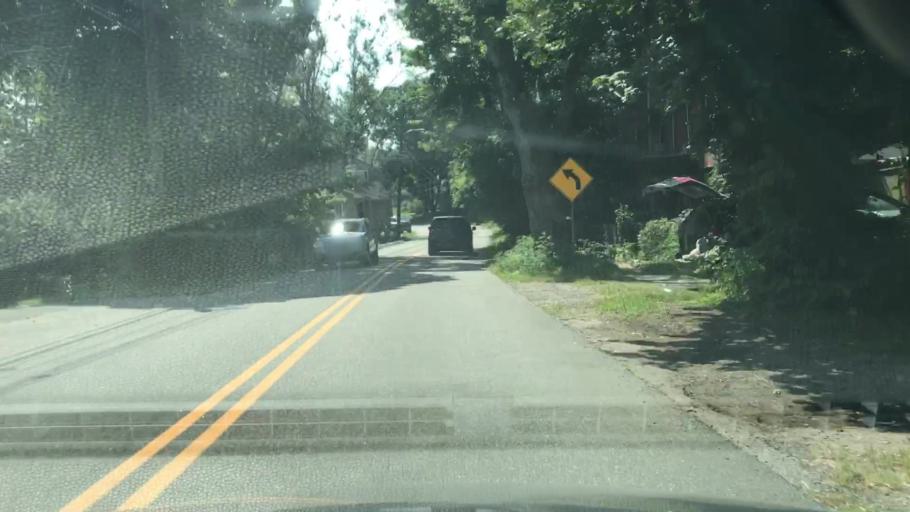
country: US
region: New Jersey
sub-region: Hunterdon County
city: Milford
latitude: 40.6106
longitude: -75.0769
